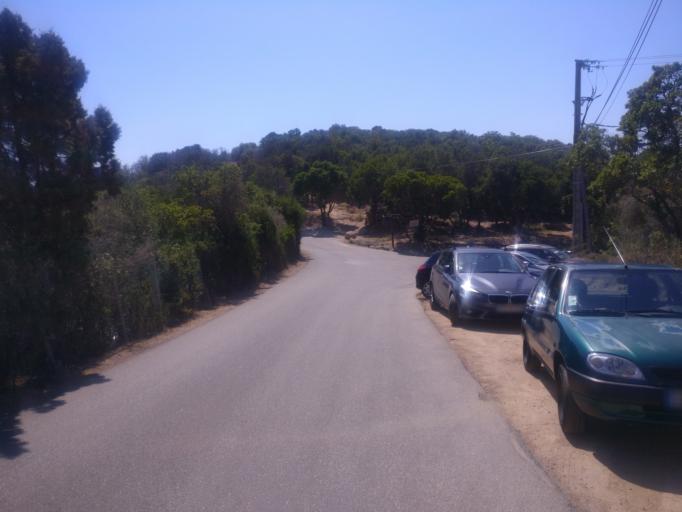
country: FR
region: Corsica
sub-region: Departement de la Corse-du-Sud
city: Pietrosella
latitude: 41.8450
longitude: 8.7602
